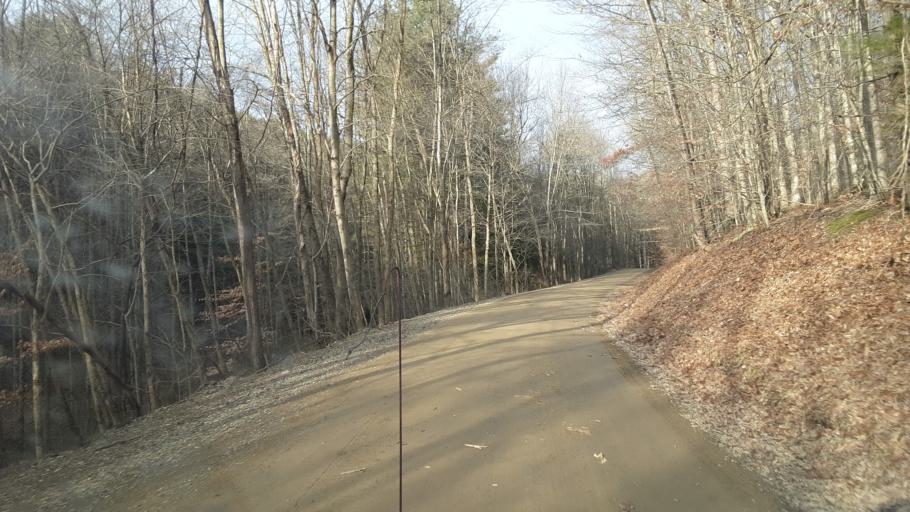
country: US
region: Ohio
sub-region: Knox County
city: Oak Hill
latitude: 40.4307
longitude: -82.2085
